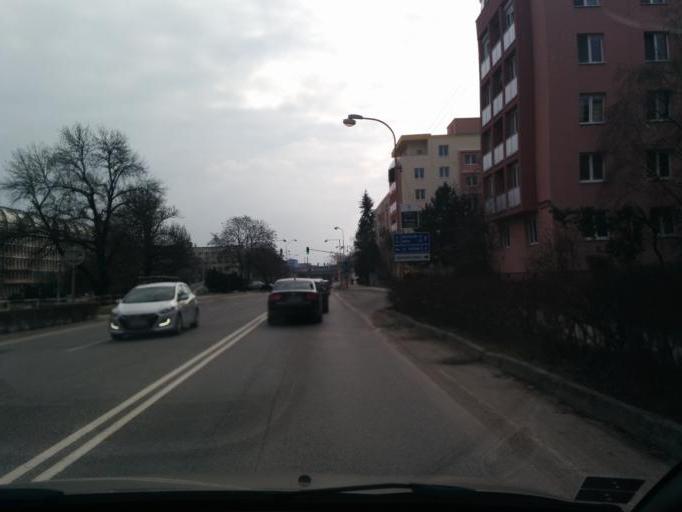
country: SK
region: Trnavsky
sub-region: Okres Trnava
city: Trnava
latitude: 48.3733
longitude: 17.5838
